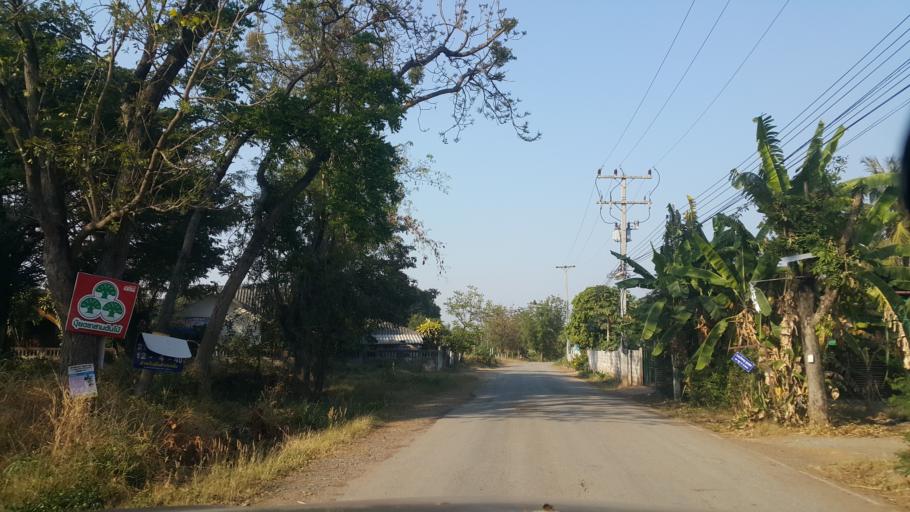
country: TH
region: Nakhon Ratchasima
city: Chakkarat
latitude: 15.0682
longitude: 102.3952
